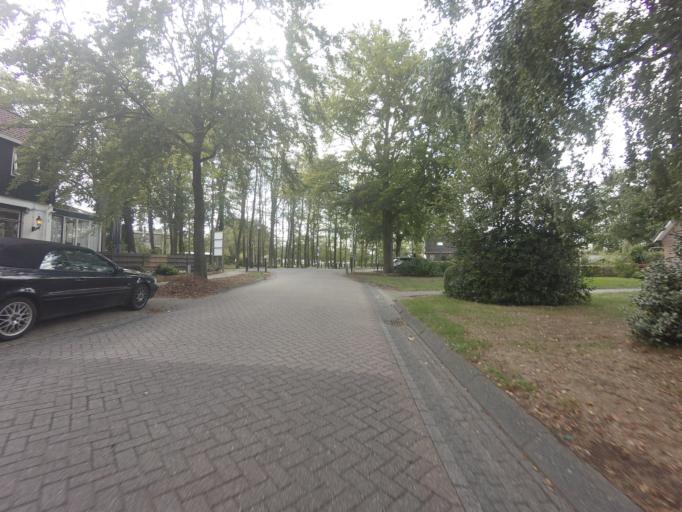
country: NL
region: Drenthe
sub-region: Gemeente Westerveld
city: Dwingeloo
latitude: 52.9546
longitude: 6.3387
